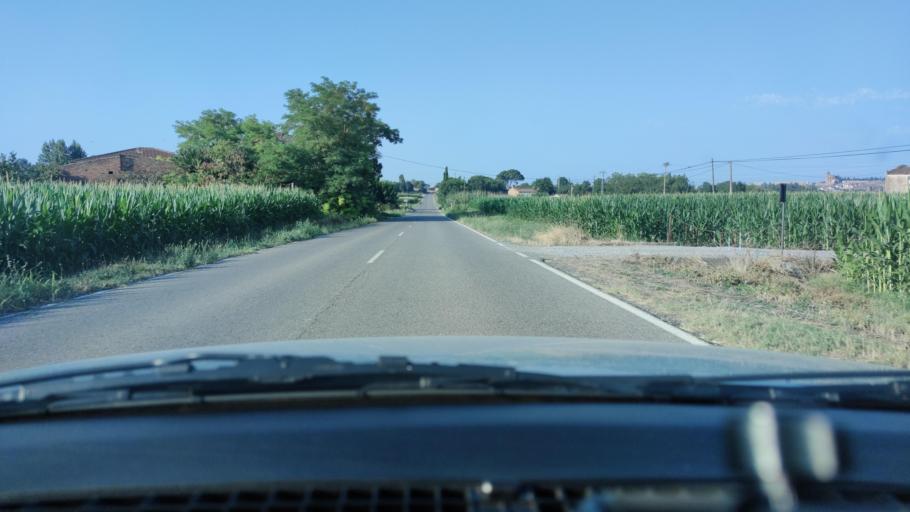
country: ES
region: Catalonia
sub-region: Provincia de Lleida
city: Balaguer
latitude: 41.8044
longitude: 0.8263
